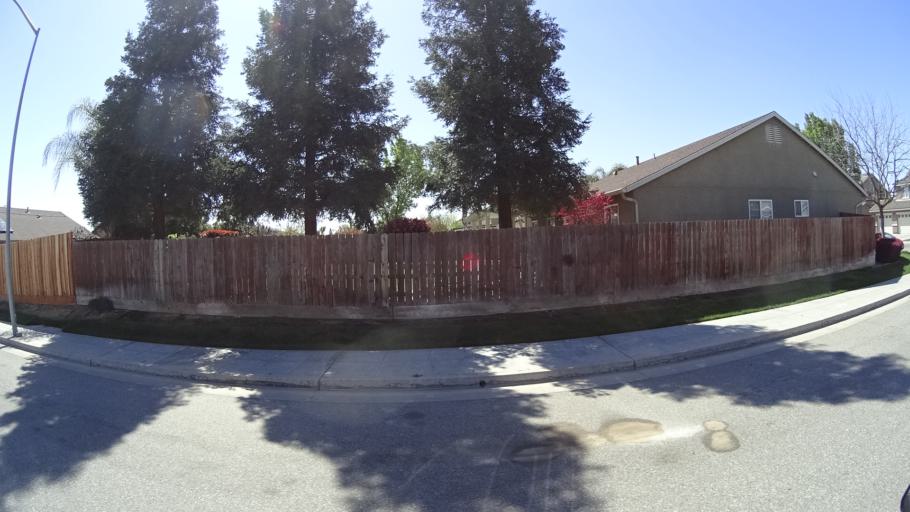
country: US
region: California
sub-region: Fresno County
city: West Park
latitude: 36.7841
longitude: -119.8915
